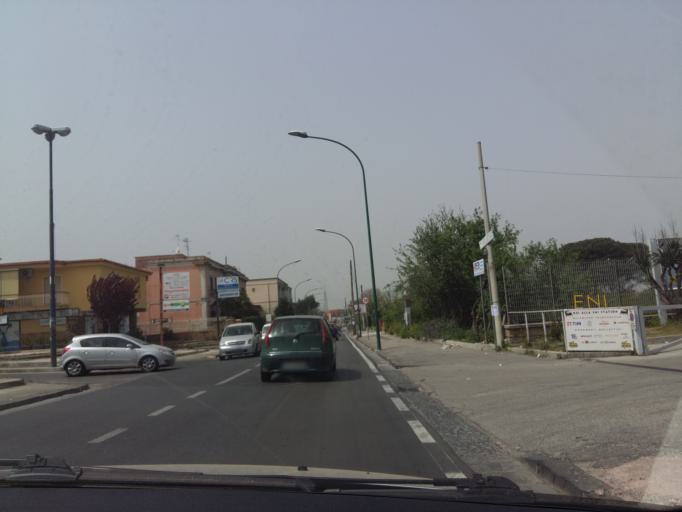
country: IT
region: Campania
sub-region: Provincia di Napoli
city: Mugnano di Napoli
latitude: 40.8957
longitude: 14.2144
